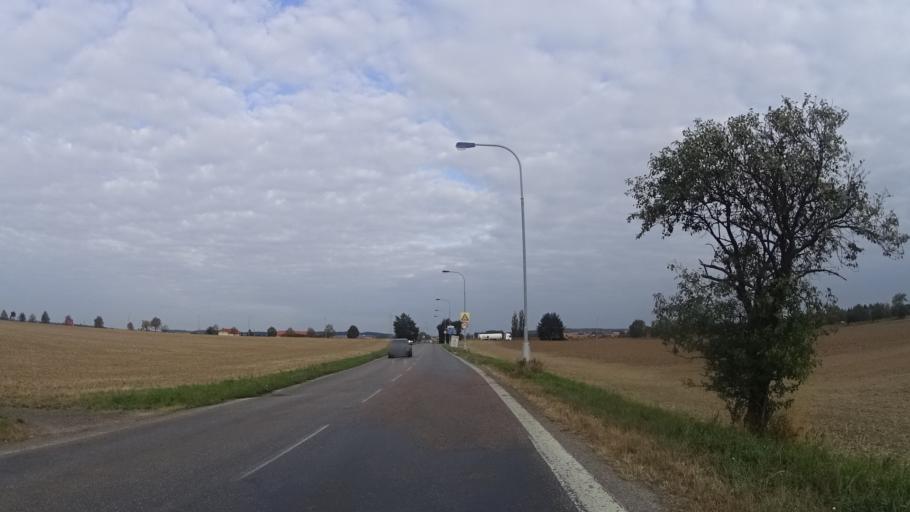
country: CZ
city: Stezery
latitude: 50.2091
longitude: 15.7851
